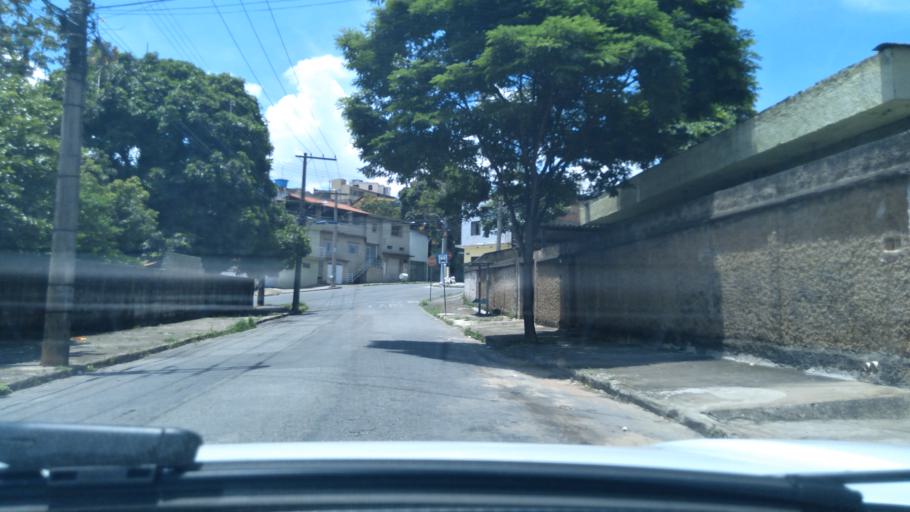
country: BR
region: Minas Gerais
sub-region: Contagem
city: Contagem
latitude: -19.9279
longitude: -44.0113
